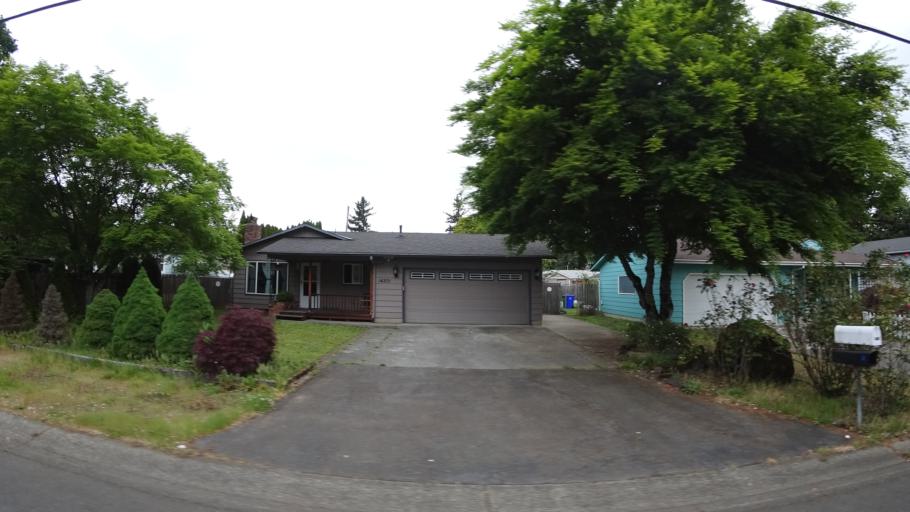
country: US
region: Oregon
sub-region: Multnomah County
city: Lents
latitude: 45.5103
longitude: -122.5169
